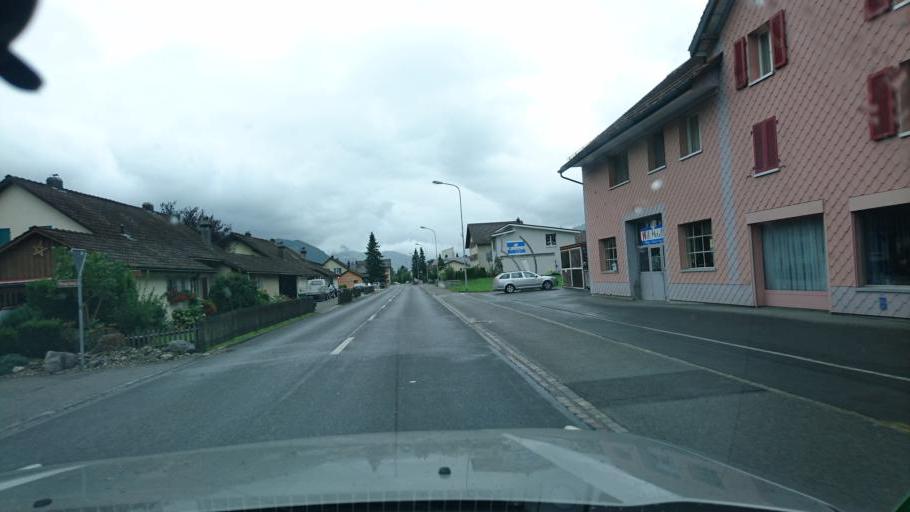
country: CH
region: Saint Gallen
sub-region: Wahlkreis Sarganserland
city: Sargans
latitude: 47.0567
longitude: 9.4143
